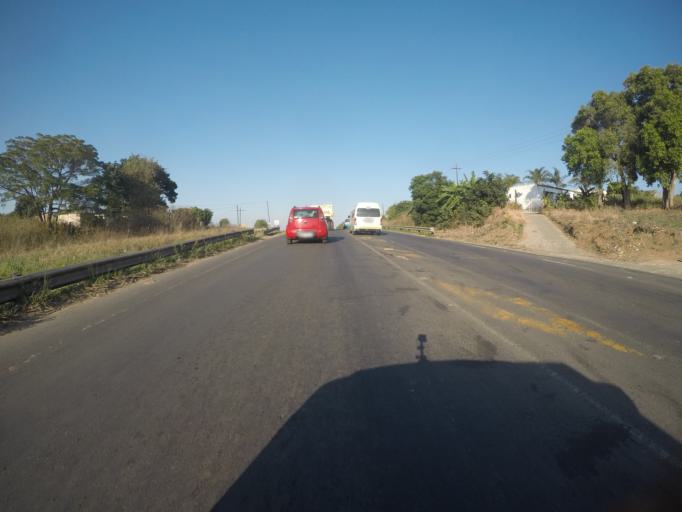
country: ZA
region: KwaZulu-Natal
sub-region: iLembe District Municipality
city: Stanger
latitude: -29.4033
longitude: 31.2506
